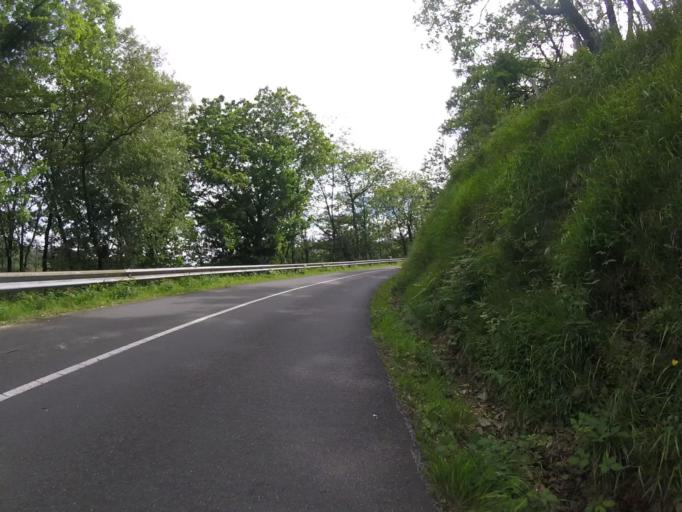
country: ES
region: Basque Country
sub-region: Provincia de Guipuzcoa
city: Errenteria
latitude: 43.2630
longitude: -1.8466
